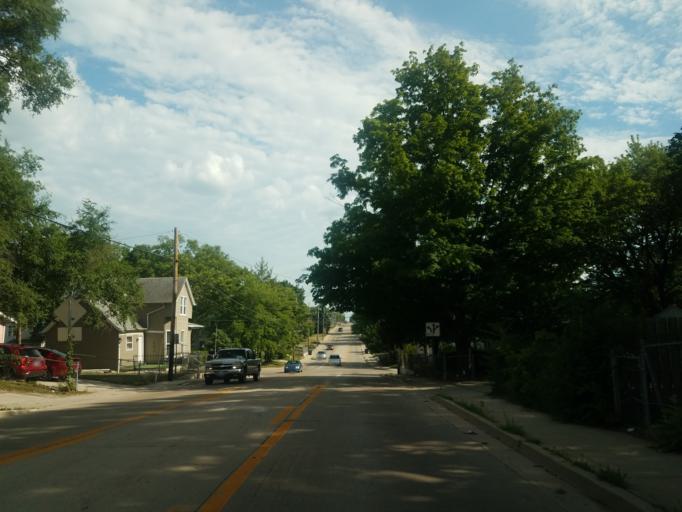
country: US
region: Illinois
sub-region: McLean County
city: Bloomington
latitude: 40.4774
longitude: -89.0066
